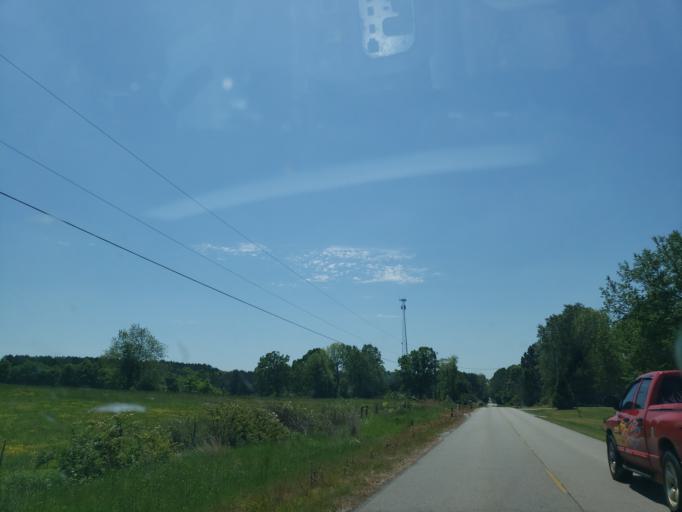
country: US
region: Alabama
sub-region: Madison County
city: Harvest
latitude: 34.9255
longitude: -86.7298
